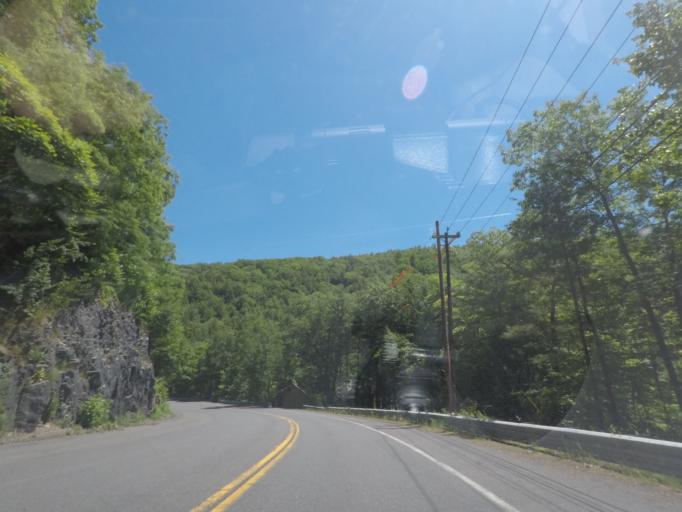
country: US
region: Massachusetts
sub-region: Berkshire County
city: Becket
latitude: 42.2734
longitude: -72.9965
